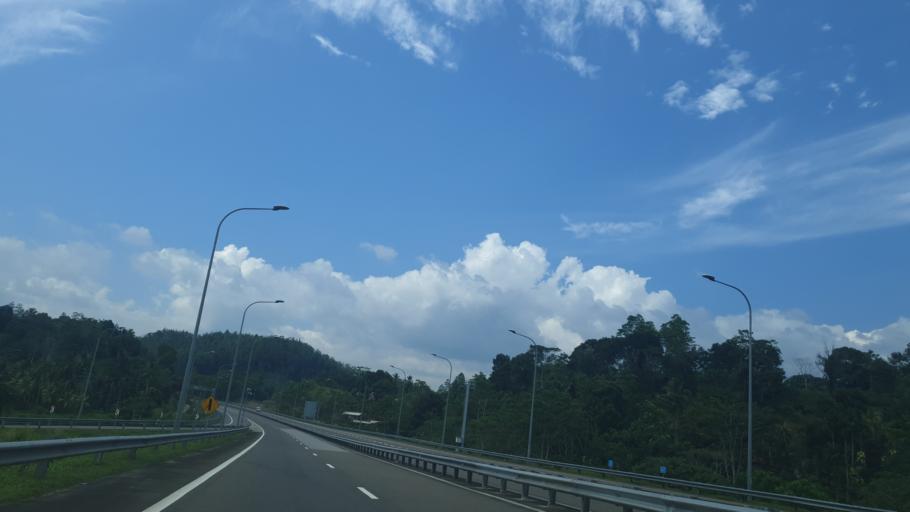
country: LK
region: Southern
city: Weligama
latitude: 6.0359
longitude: 80.3642
